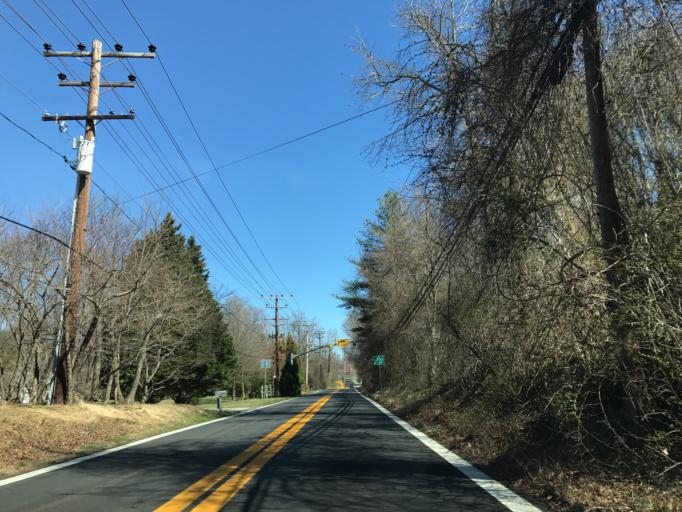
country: US
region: Maryland
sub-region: Anne Arundel County
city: Cape Saint Claire
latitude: 39.0197
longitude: -76.4655
